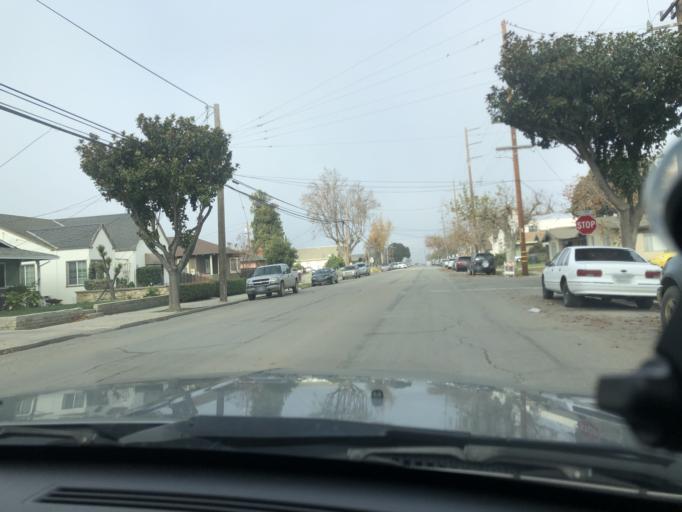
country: US
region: California
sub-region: Monterey County
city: King City
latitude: 36.2161
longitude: -121.1289
